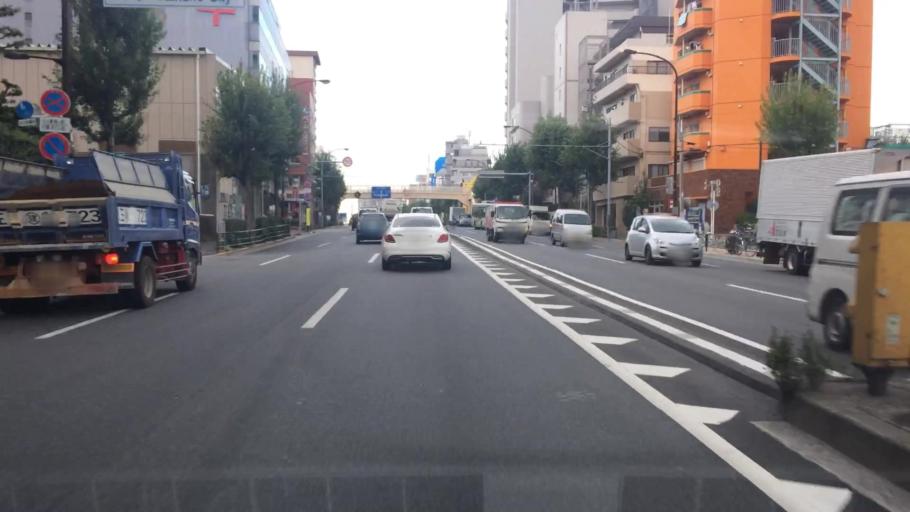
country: JP
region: Tokyo
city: Tokyo
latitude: 35.7266
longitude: 139.6540
